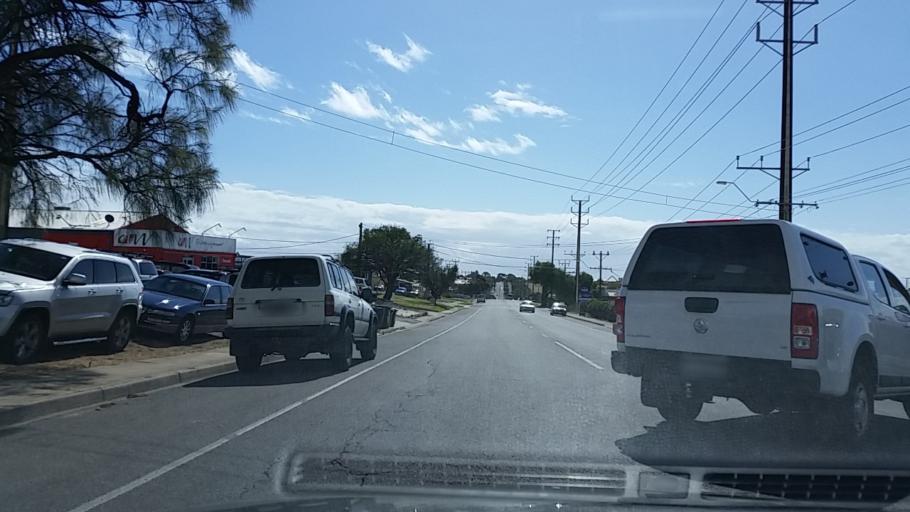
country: AU
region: South Australia
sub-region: Onkaparinga
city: Morphett Vale
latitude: -35.1170
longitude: 138.4975
